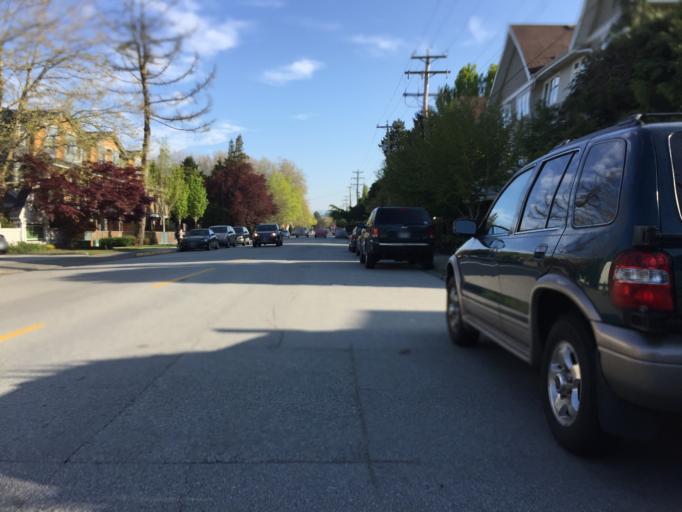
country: CA
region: British Columbia
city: Richmond
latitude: 49.1584
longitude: -123.1436
